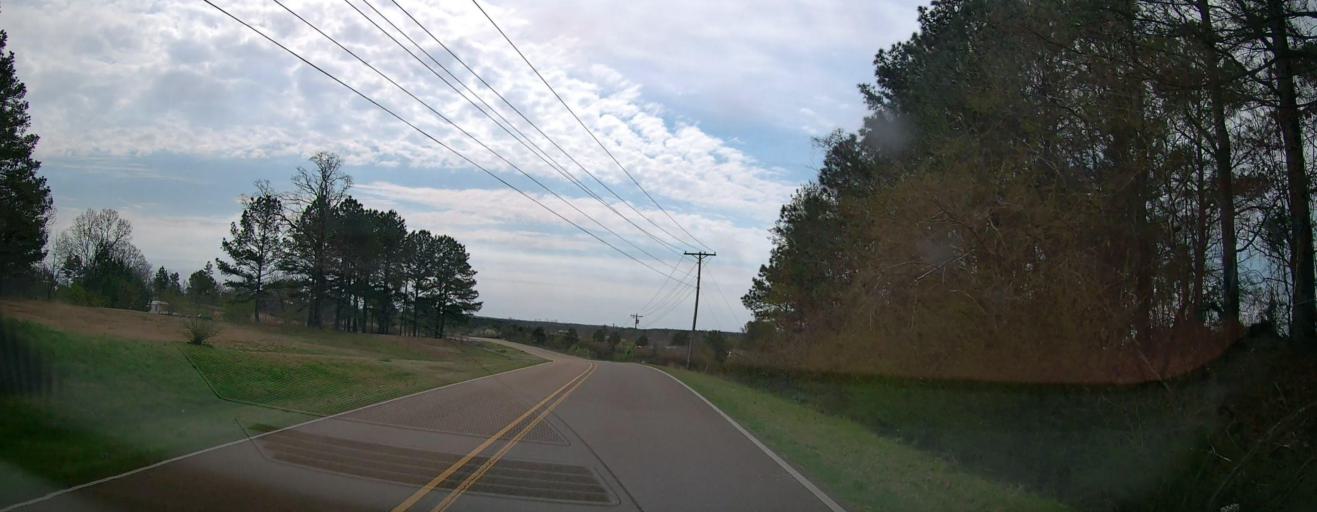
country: US
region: Mississippi
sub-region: Marshall County
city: Holly Springs
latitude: 34.7538
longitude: -89.4298
